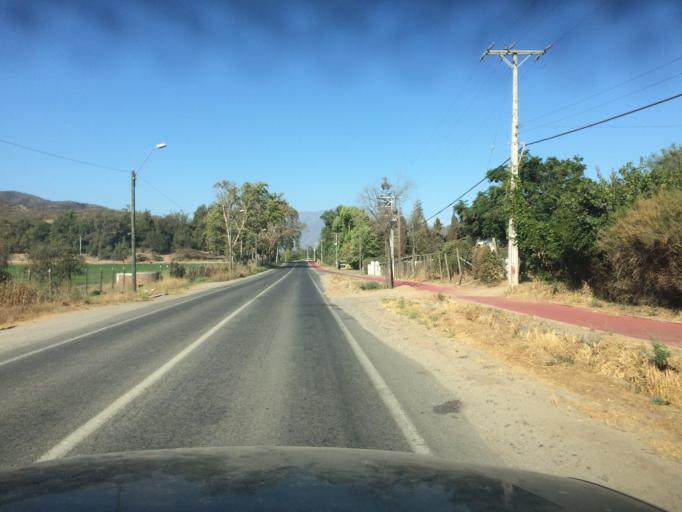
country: CL
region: Santiago Metropolitan
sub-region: Provincia de Melipilla
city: Melipilla
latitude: -33.4911
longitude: -71.1498
